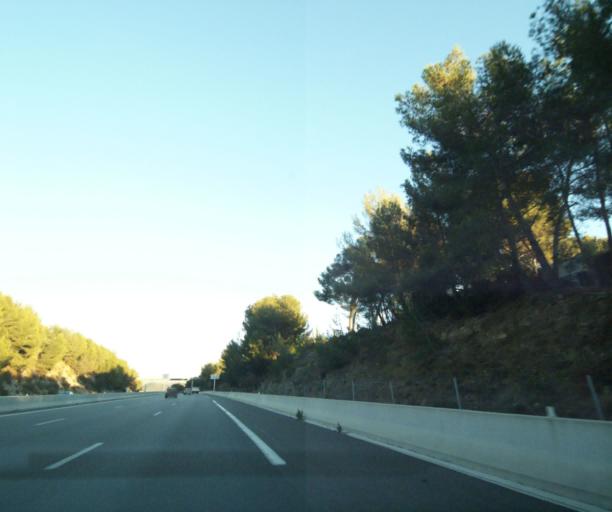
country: FR
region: Provence-Alpes-Cote d'Azur
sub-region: Departement du Var
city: Saint-Cyr-sur-Mer
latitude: 43.1926
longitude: 5.6774
